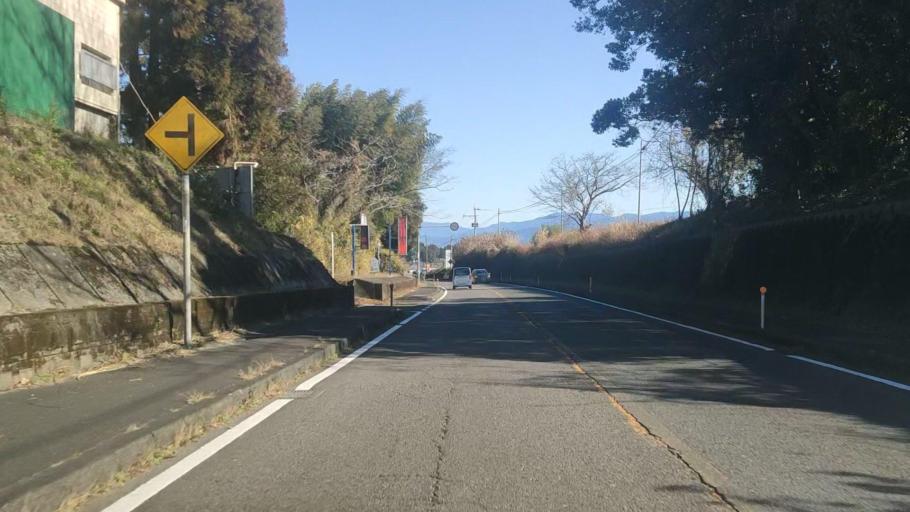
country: JP
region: Kagoshima
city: Sueyoshicho-ninokata
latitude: 31.7006
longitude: 131.0141
